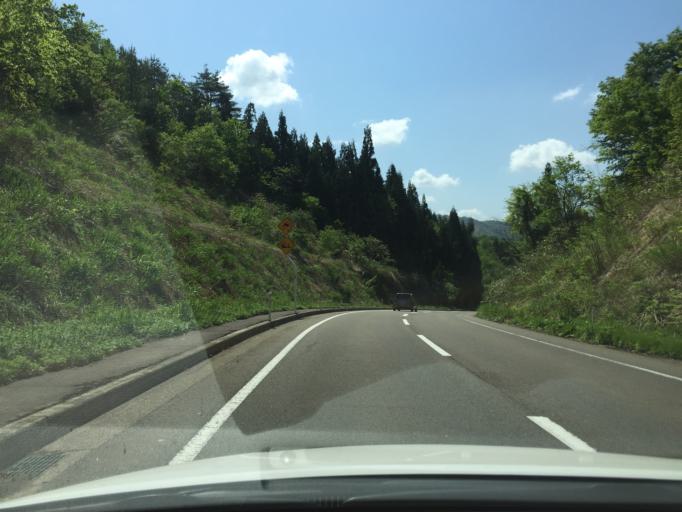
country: JP
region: Niigata
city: Kamo
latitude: 37.5836
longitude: 139.0927
